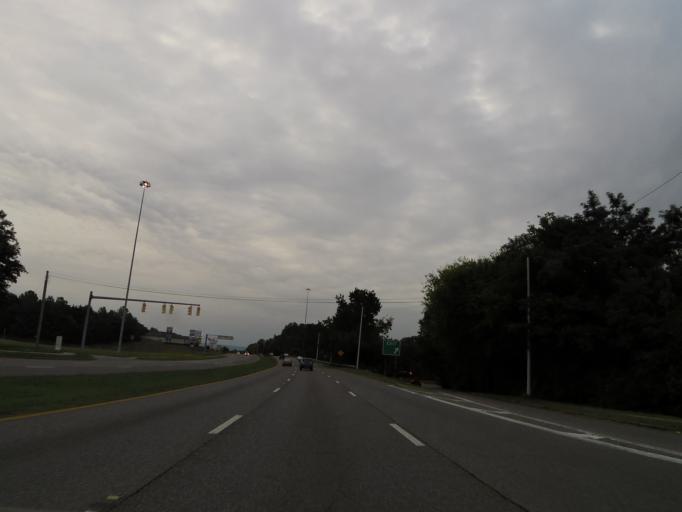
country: US
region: Alabama
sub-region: Madison County
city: Redstone Arsenal
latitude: 34.7355
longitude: -86.6470
